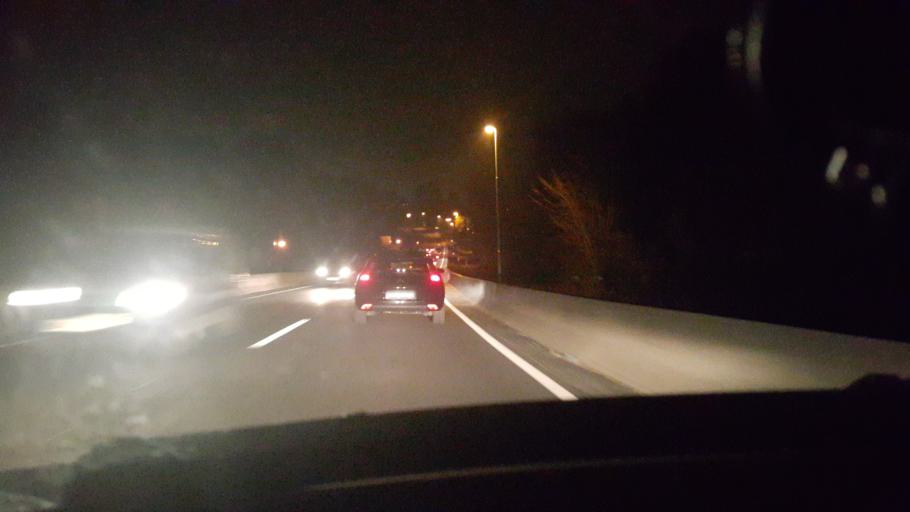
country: SI
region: Maribor
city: Kamnica
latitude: 46.5697
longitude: 15.6187
